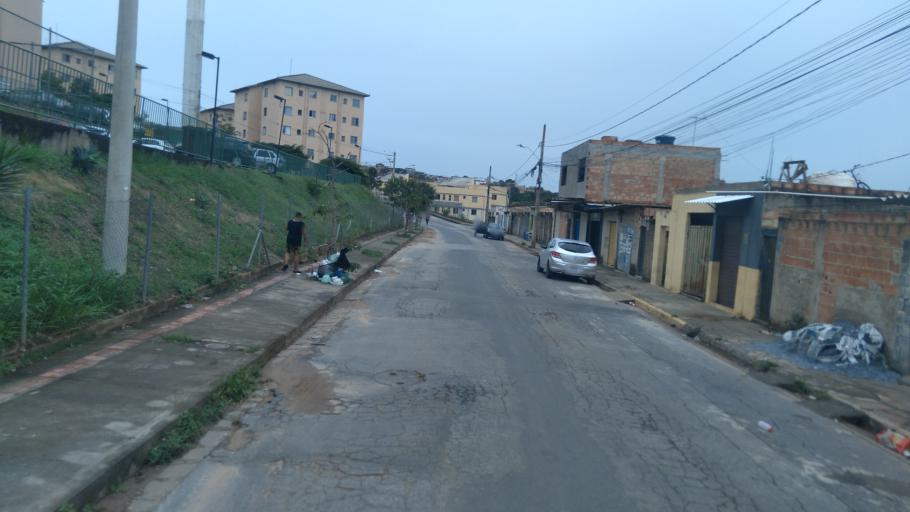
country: BR
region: Minas Gerais
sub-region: Belo Horizonte
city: Belo Horizonte
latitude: -19.9103
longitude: -43.8797
